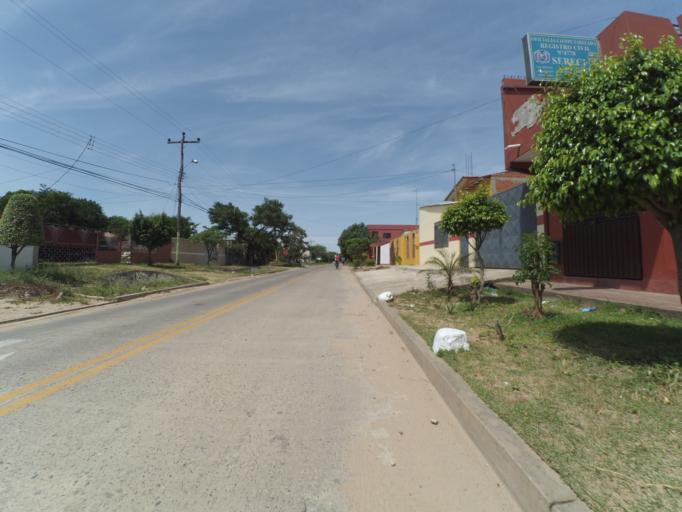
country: BO
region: Santa Cruz
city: Santa Cruz de la Sierra
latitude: -17.8214
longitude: -63.2238
